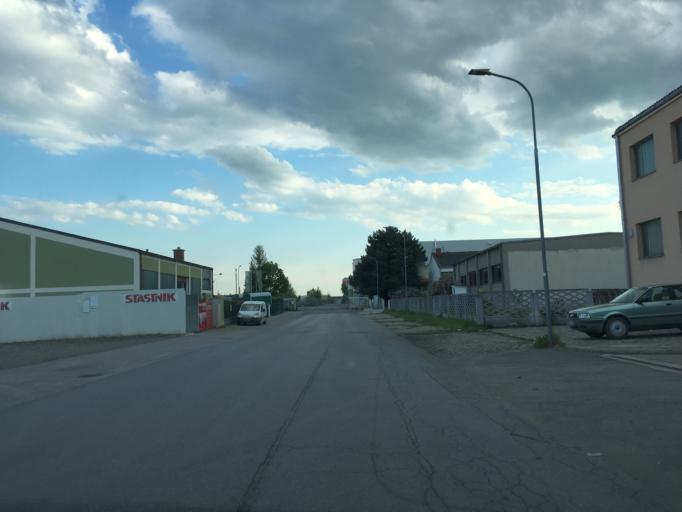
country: AT
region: Lower Austria
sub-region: Politischer Bezirk Wien-Umgebung
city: Gerasdorf bei Wien
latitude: 48.2828
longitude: 16.4814
